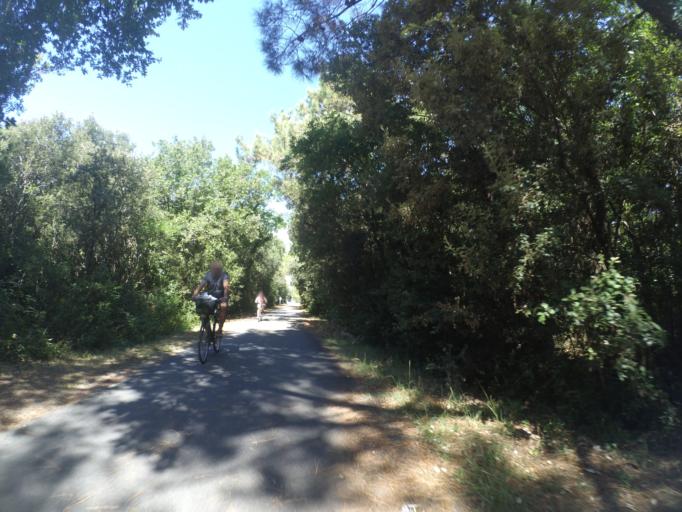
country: FR
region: Poitou-Charentes
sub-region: Departement de la Charente-Maritime
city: Les Mathes
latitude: 45.6791
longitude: -1.1559
